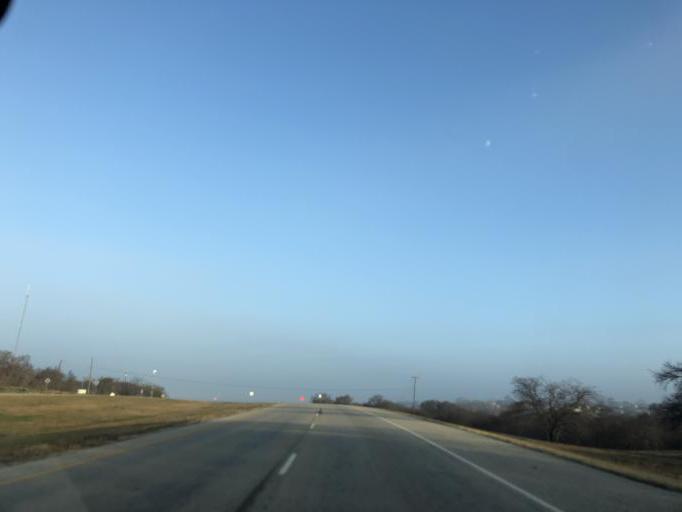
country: US
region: Texas
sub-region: Dallas County
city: Cedar Hill
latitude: 32.6386
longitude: -96.9720
